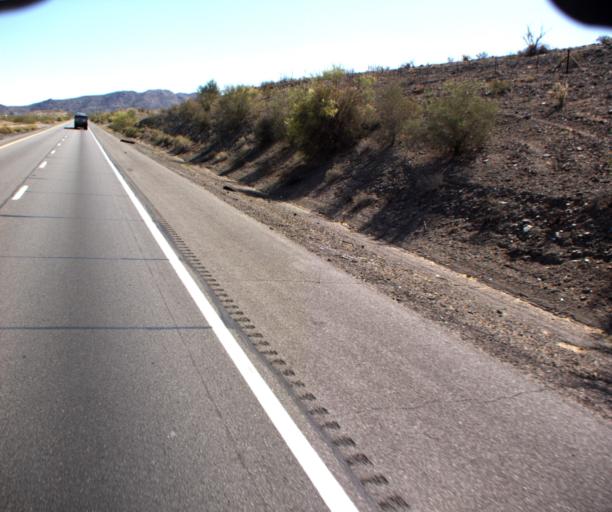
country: US
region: Arizona
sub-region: La Paz County
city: Ehrenberg
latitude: 33.6298
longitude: -114.4133
